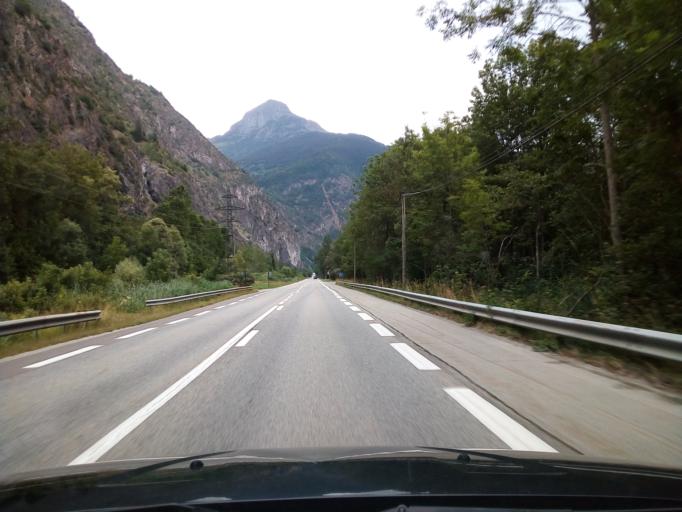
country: FR
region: Rhone-Alpes
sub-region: Departement de l'Isere
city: Huez
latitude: 45.0441
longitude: 6.0578
